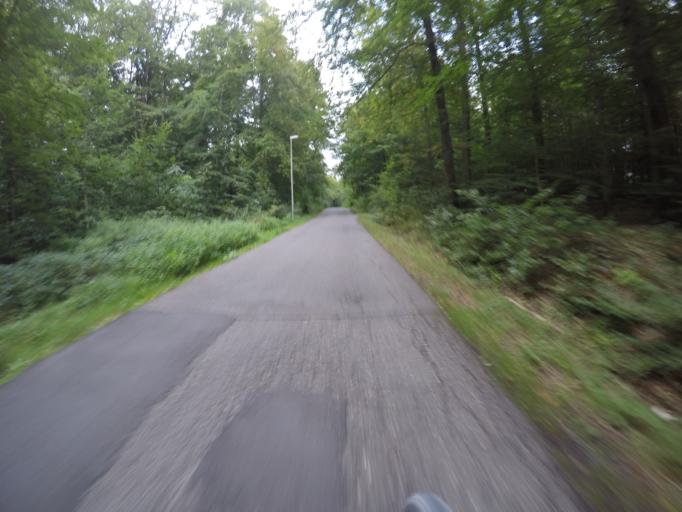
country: DE
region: Baden-Wuerttemberg
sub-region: Regierungsbezirk Stuttgart
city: Gerlingen
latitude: 48.7400
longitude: 9.0862
